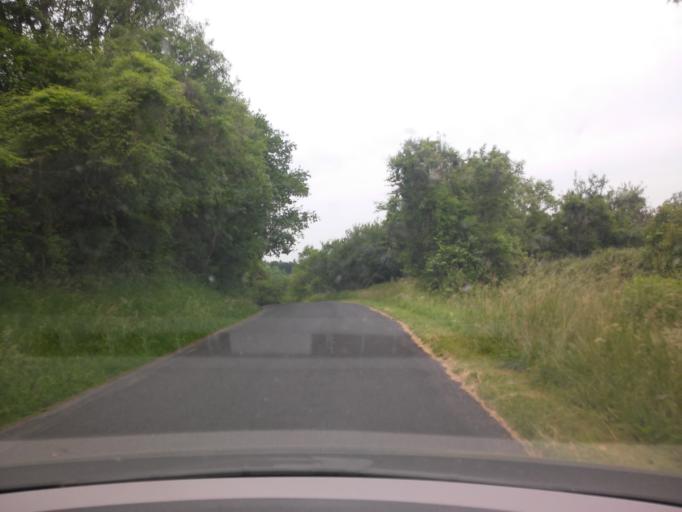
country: FR
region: Lorraine
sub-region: Departement de la Meuse
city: Vignot
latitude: 48.7999
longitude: 5.6638
